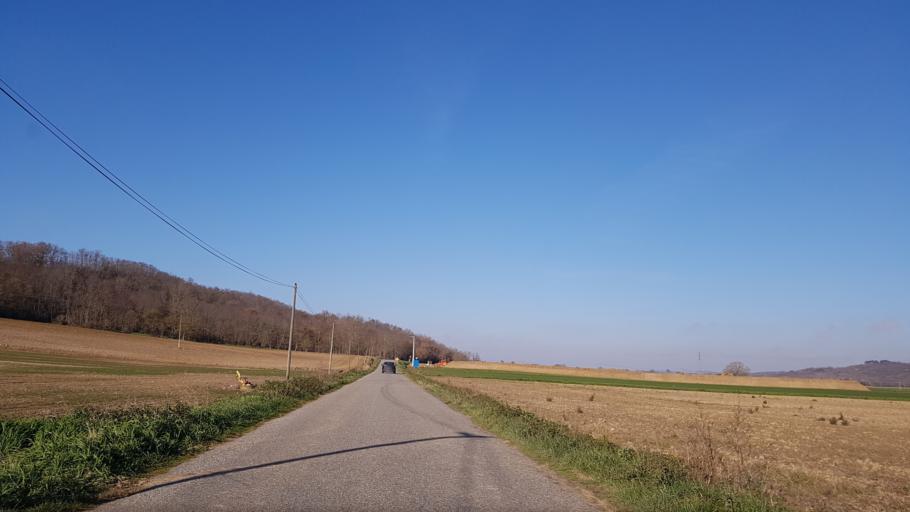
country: FR
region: Midi-Pyrenees
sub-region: Departement de l'Ariege
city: La Tour-du-Crieu
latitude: 43.1167
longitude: 1.7223
